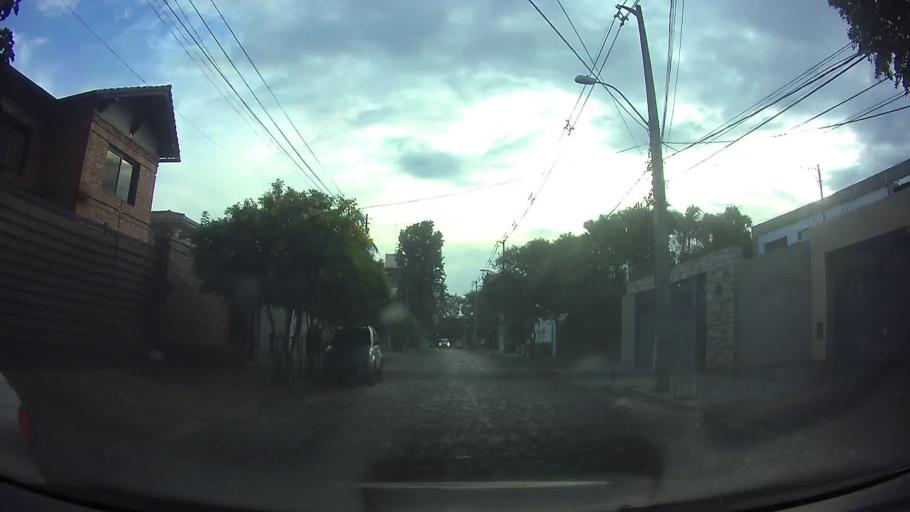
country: PY
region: Asuncion
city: Asuncion
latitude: -25.2802
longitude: -57.5668
